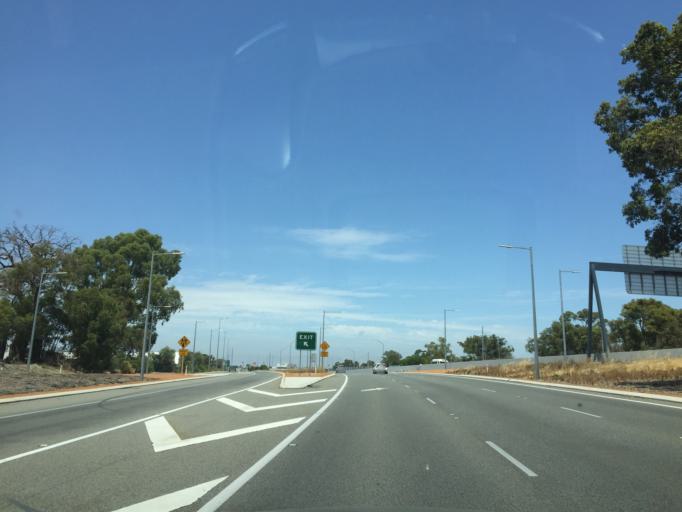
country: AU
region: Western Australia
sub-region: Belmont
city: Kewdale
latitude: -31.9690
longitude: 115.9530
